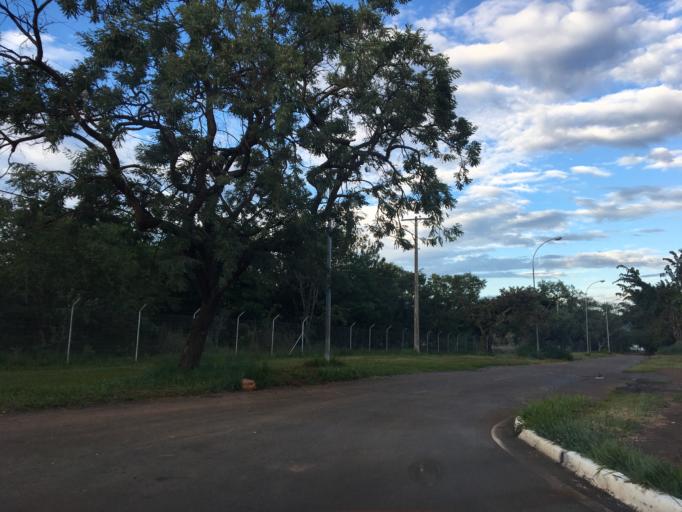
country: BR
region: Federal District
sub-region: Brasilia
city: Brasilia
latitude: -15.8041
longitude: -47.8351
